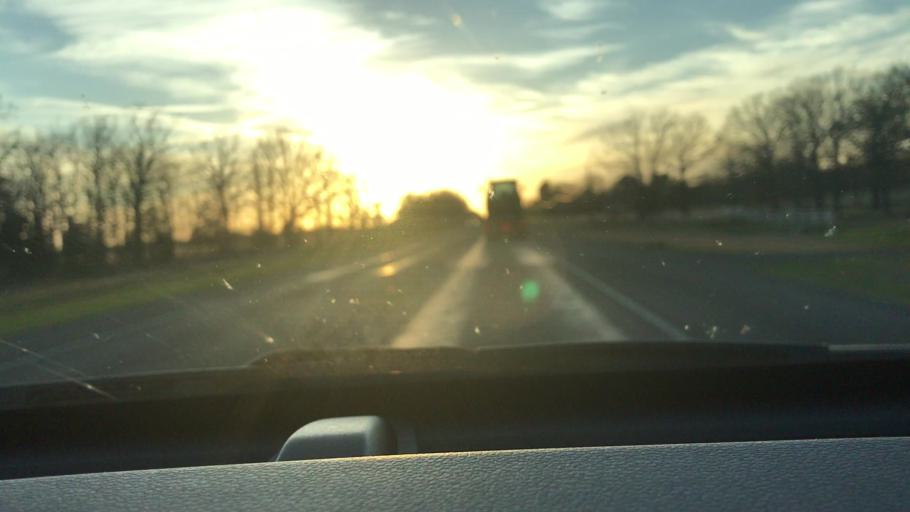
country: US
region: Texas
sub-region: Lamar County
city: Blossom
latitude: 33.6662
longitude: -95.3434
